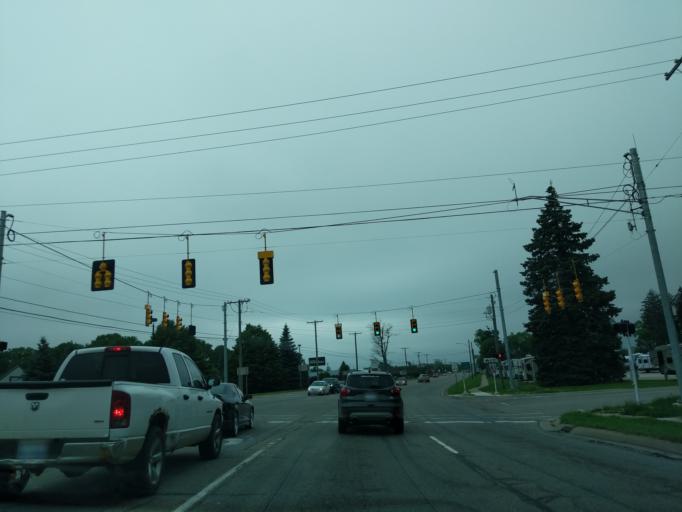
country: US
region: Michigan
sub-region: Branch County
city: Coldwater
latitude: 41.9343
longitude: -84.9610
